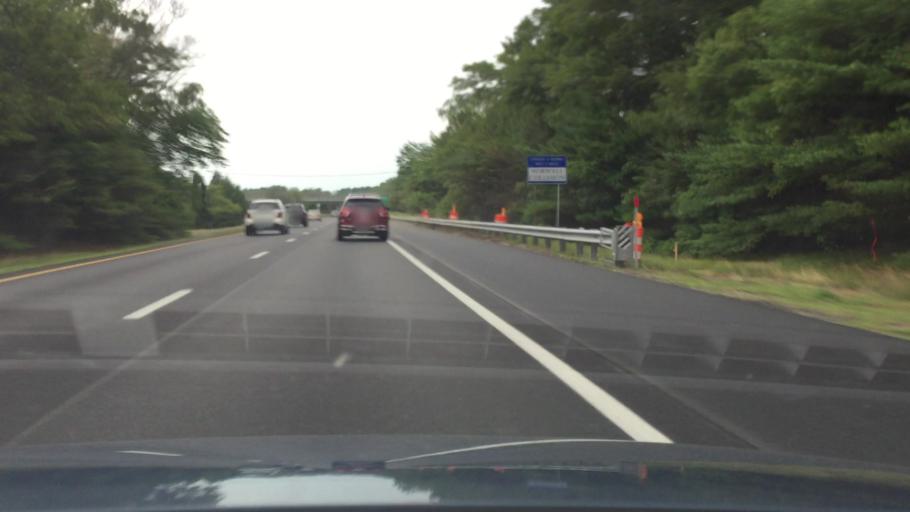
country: US
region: Massachusetts
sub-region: Plymouth County
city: Kingston
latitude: 42.0344
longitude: -70.7244
